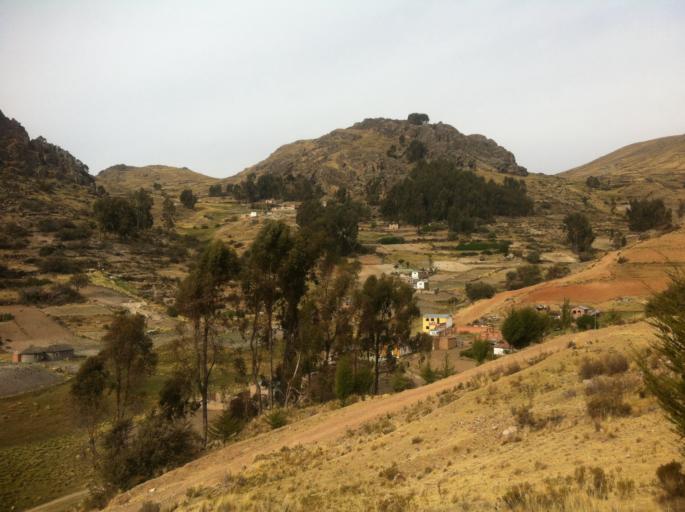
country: PE
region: Puno
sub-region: Yunguyo
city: Yunguyo
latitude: -16.1881
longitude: -69.0817
